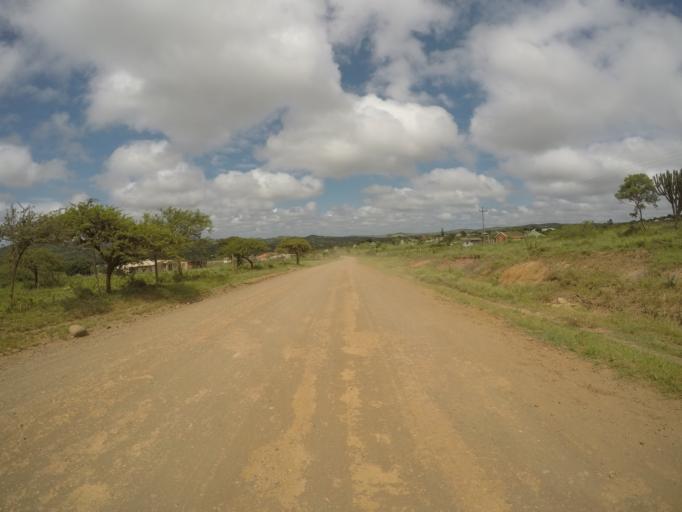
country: ZA
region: KwaZulu-Natal
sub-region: uThungulu District Municipality
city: Empangeni
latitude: -28.5802
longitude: 31.8473
